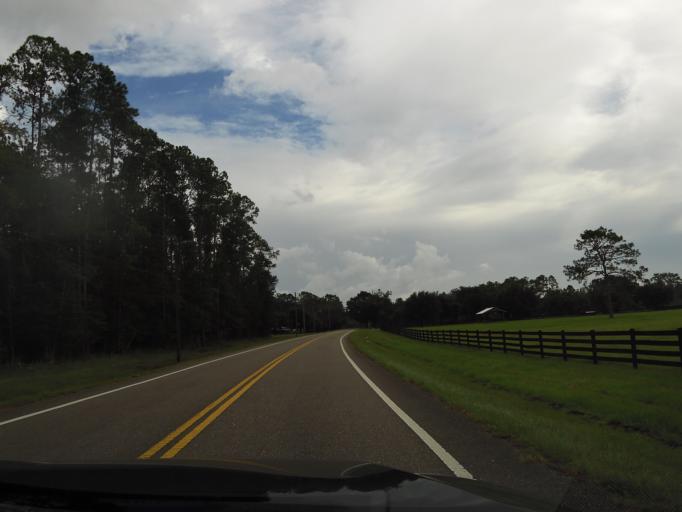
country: US
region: Florida
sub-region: Duval County
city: Baldwin
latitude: 30.3645
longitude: -81.9214
